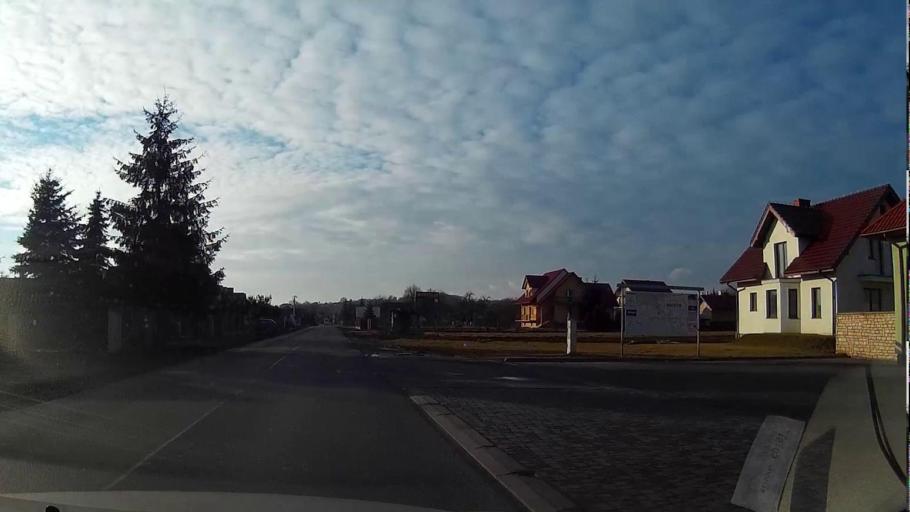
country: PL
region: Lesser Poland Voivodeship
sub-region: Powiat krakowski
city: Mnikow
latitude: 50.0599
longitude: 19.7303
